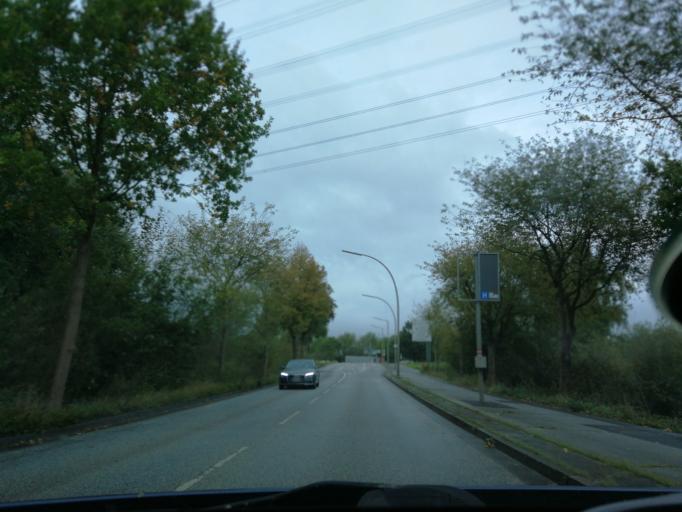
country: DE
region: Hamburg
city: Harburg
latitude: 53.4750
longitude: 9.9377
